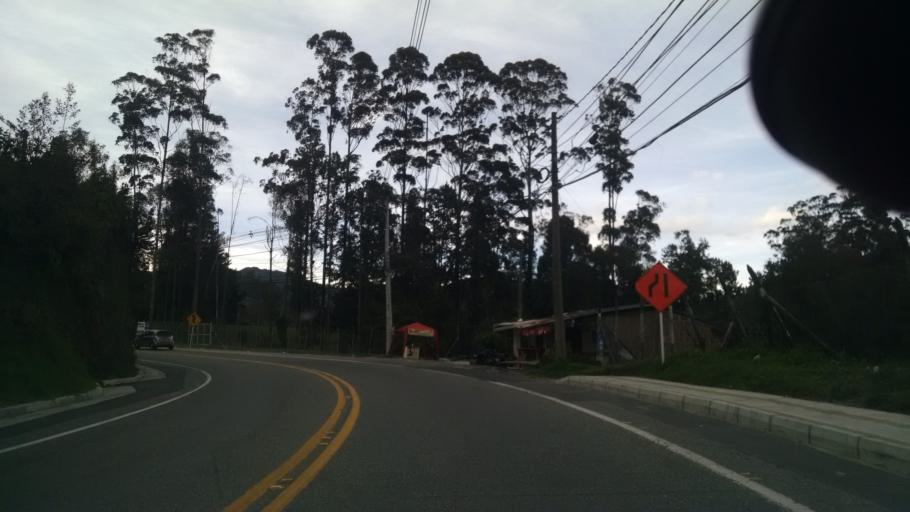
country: CO
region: Antioquia
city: El Retiro
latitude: 6.1106
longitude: -75.5006
